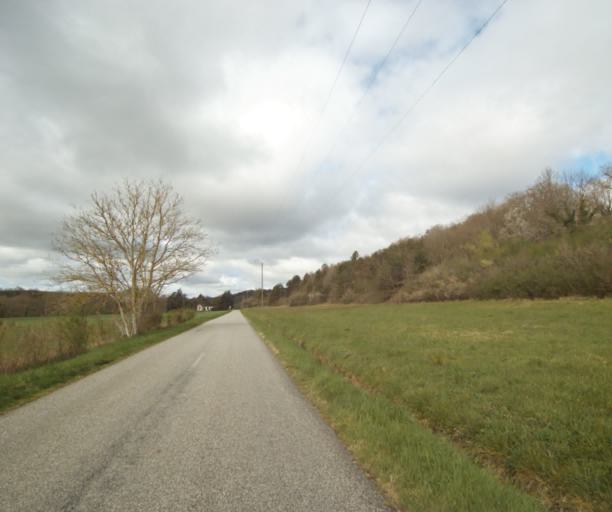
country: FR
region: Midi-Pyrenees
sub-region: Departement de l'Ariege
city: Saverdun
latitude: 43.2270
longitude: 1.5498
